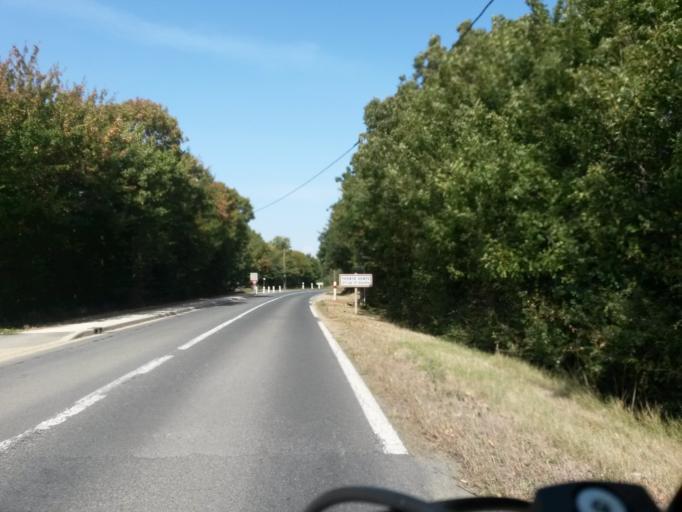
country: FR
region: Poitou-Charentes
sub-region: Departement de la Charente-Maritime
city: Saint-Xandre
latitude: 46.2130
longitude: -1.0944
